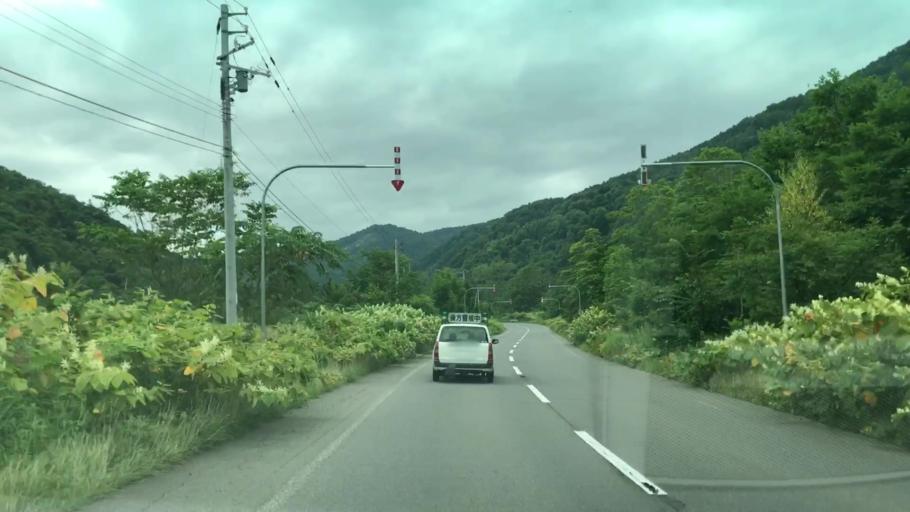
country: JP
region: Hokkaido
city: Yoichi
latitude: 43.0256
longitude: 140.8665
